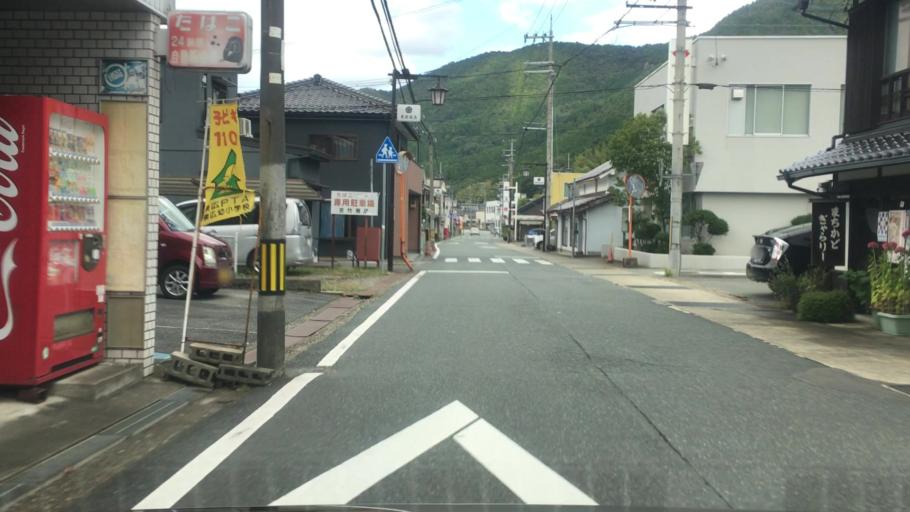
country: JP
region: Hyogo
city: Sasayama
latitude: 35.1315
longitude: 135.0767
